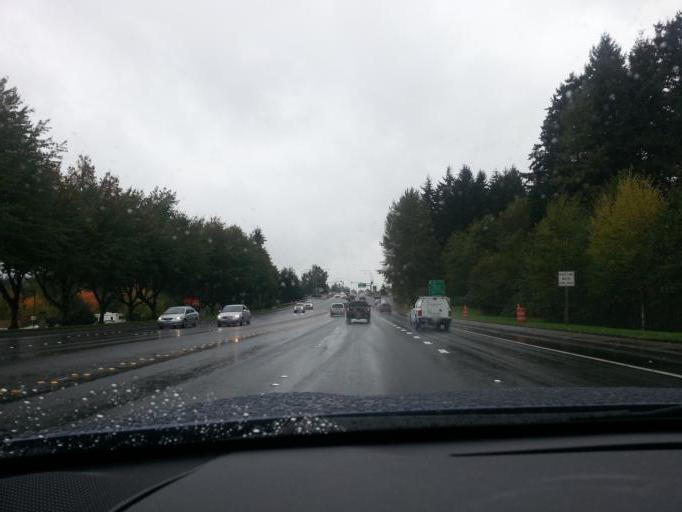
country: US
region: Washington
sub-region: King County
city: Bothell
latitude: 47.7979
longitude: -122.2125
